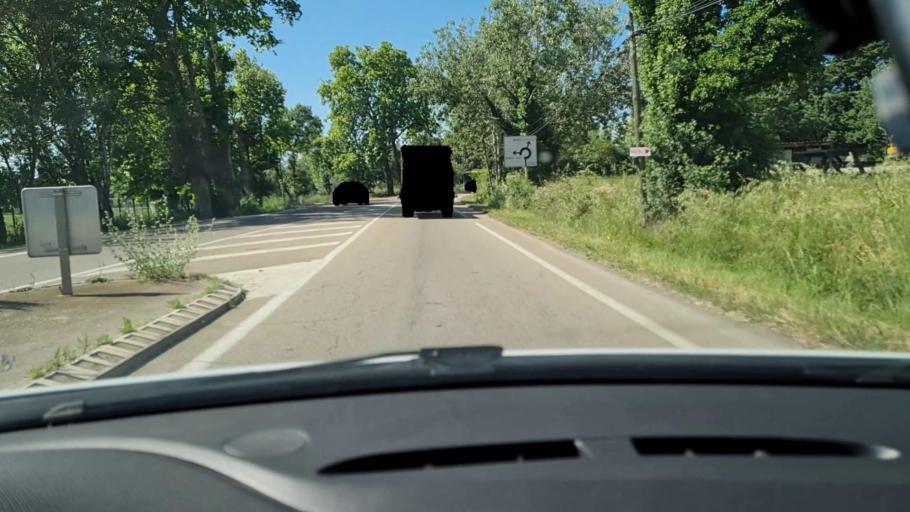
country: FR
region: Languedoc-Roussillon
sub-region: Departement du Gard
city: Caissargues
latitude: 43.7896
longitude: 4.3509
